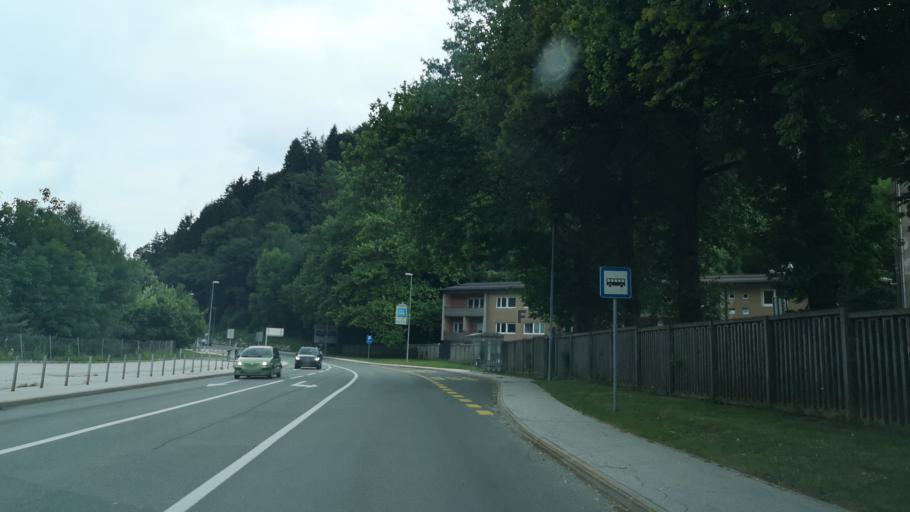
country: SI
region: Jesenice
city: Hrusica
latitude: 46.4425
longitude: 14.0361
